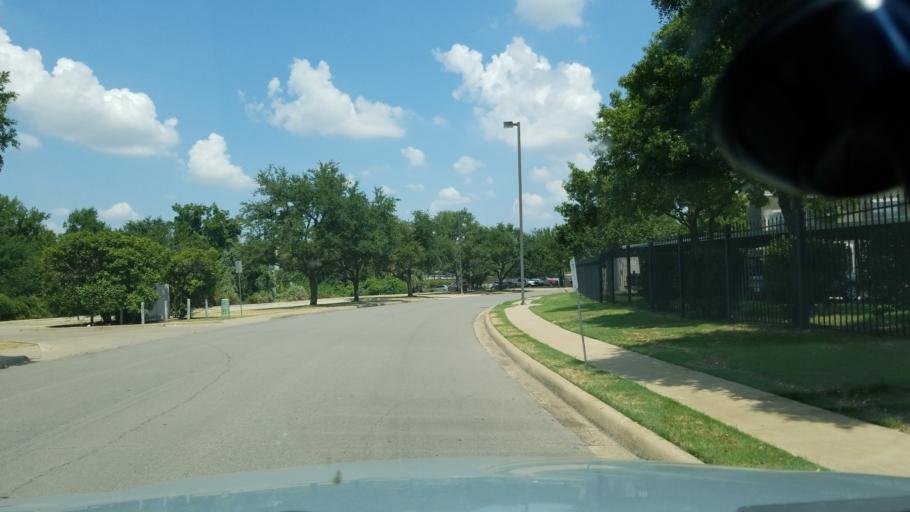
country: US
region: Texas
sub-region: Dallas County
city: Irving
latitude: 32.8579
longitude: -96.9012
